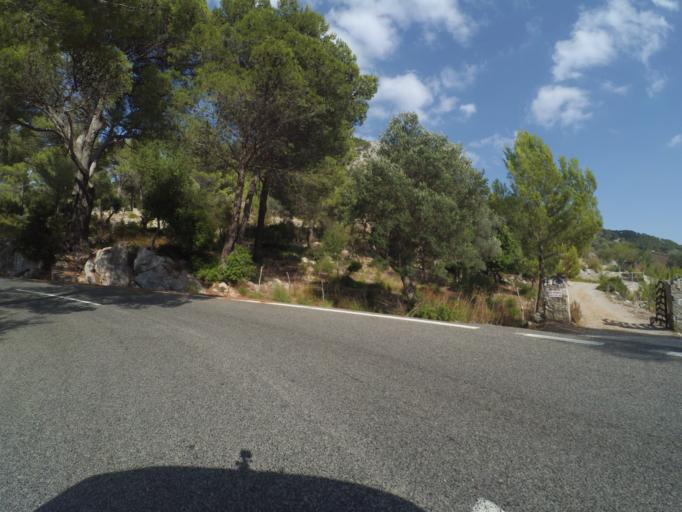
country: ES
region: Balearic Islands
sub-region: Illes Balears
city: Selva
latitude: 39.7889
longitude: 2.8934
